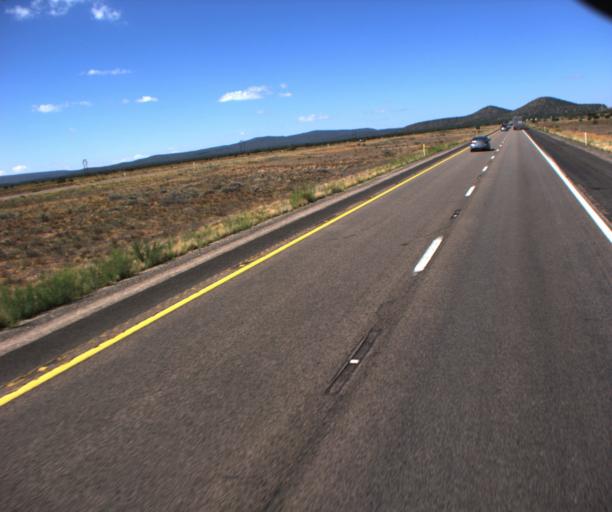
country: US
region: Arizona
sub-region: Mohave County
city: Peach Springs
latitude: 35.3088
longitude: -112.9844
